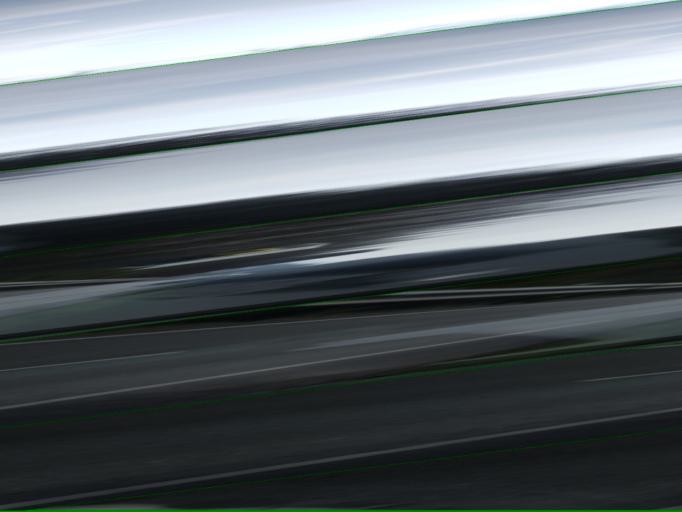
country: FR
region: Ile-de-France
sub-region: Departement des Yvelines
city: Houdan
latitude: 48.7827
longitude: 1.5833
